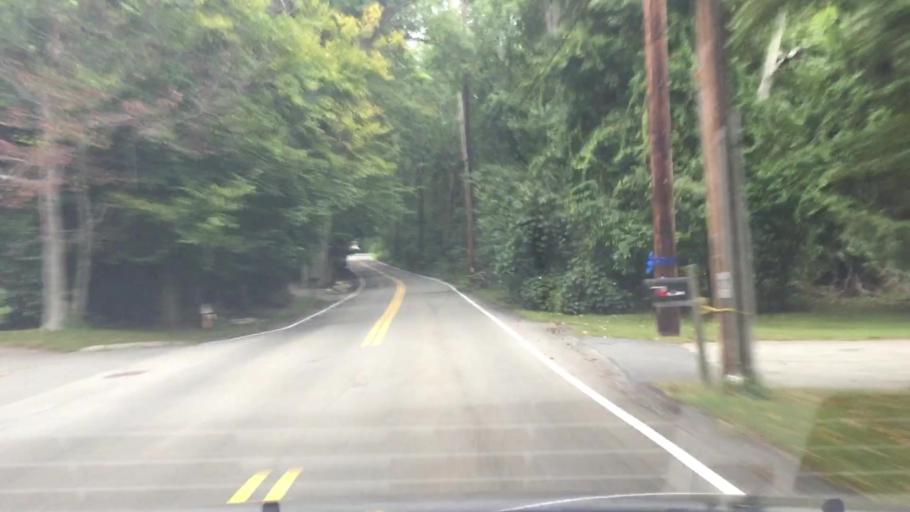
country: US
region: Massachusetts
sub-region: Essex County
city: North Andover
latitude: 42.7329
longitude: -71.1064
